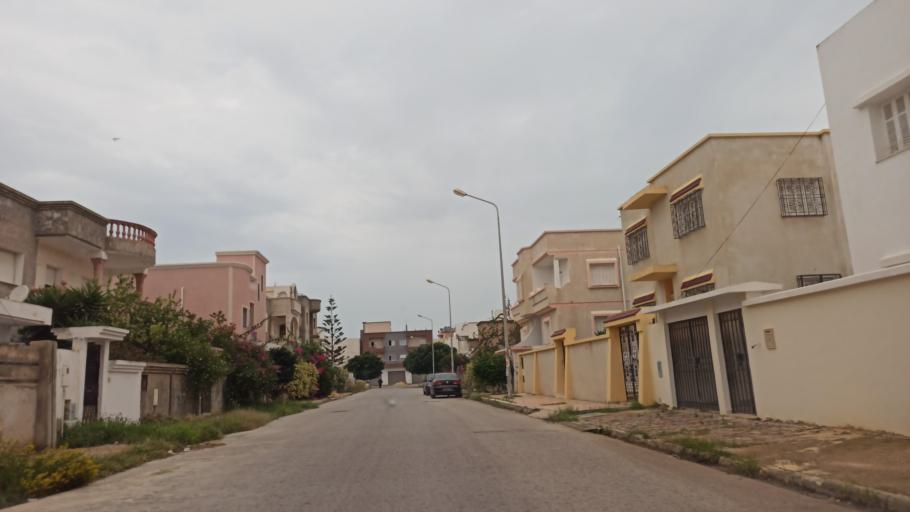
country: TN
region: Tunis
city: Hammam-Lif
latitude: 36.7074
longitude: 10.4144
